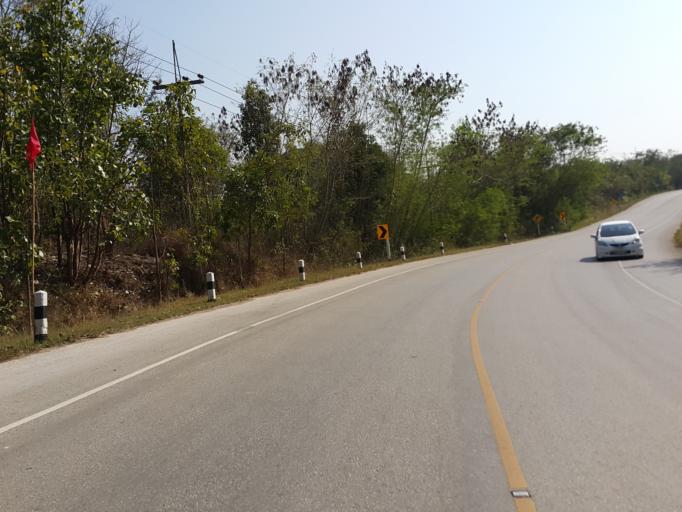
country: TH
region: Lampang
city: Chae Hom
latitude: 18.7665
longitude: 99.5738
